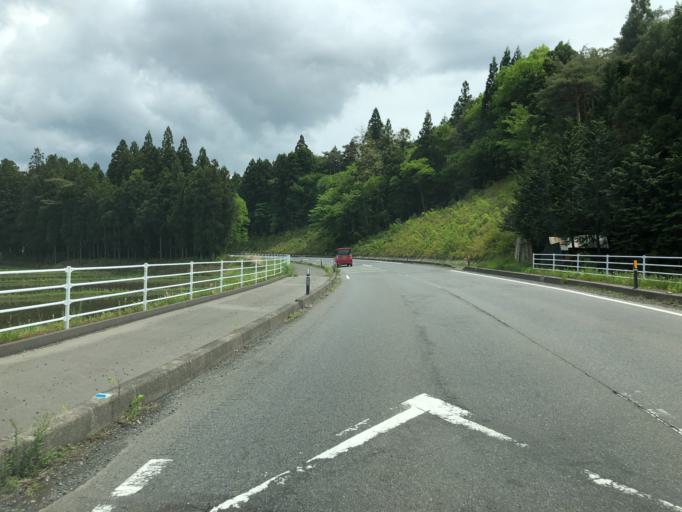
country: JP
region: Fukushima
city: Ishikawa
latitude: 37.0707
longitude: 140.3637
